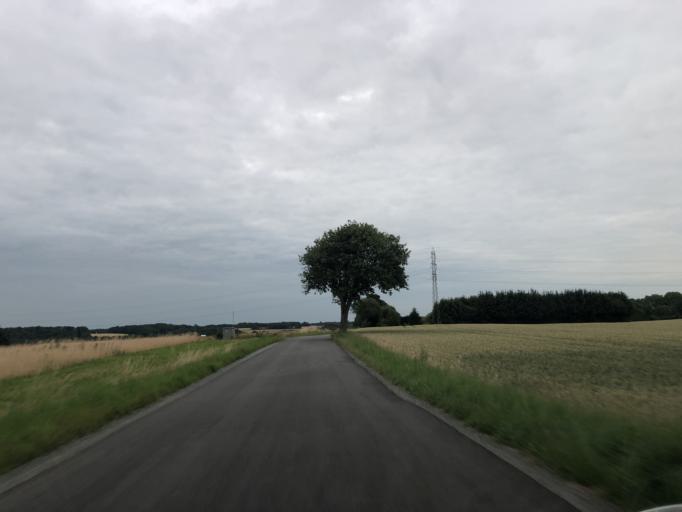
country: DK
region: South Denmark
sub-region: Vejle Kommune
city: Jelling
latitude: 55.7232
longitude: 9.3958
